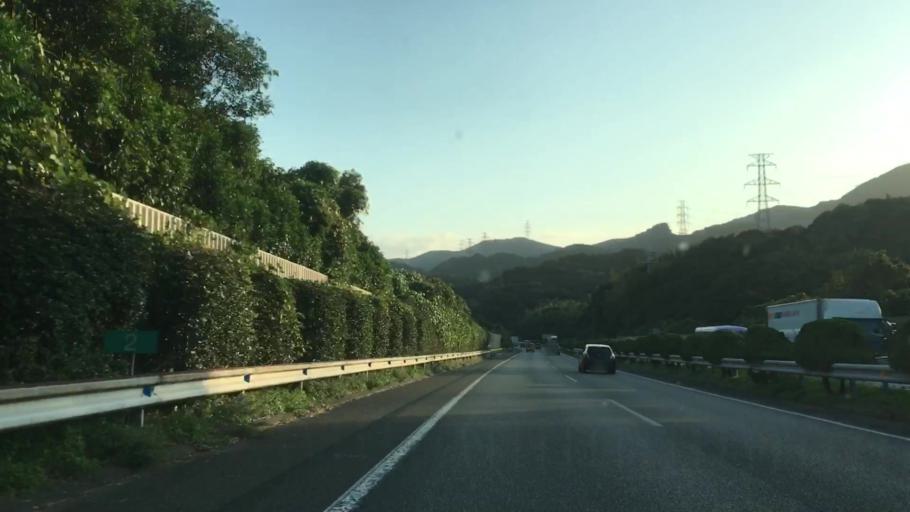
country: JP
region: Yamaguchi
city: Shimonoseki
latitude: 33.9085
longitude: 130.9741
